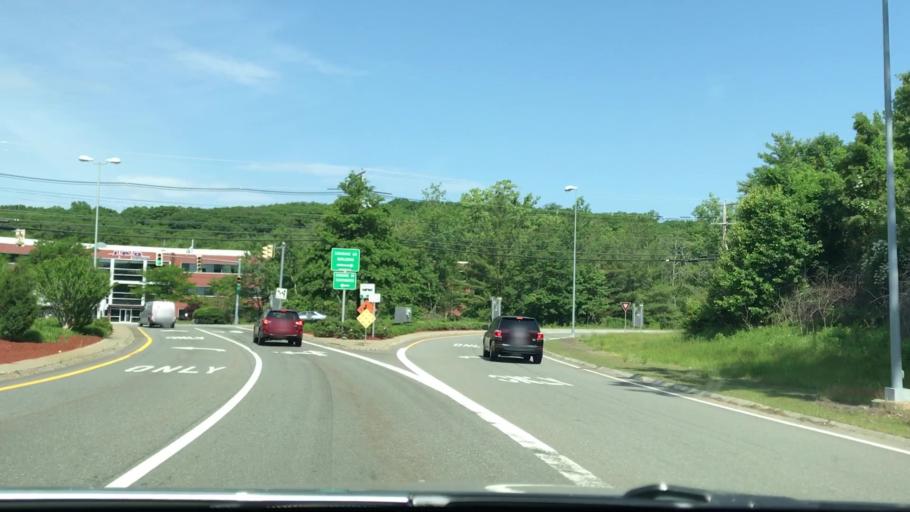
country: US
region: Massachusetts
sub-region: Middlesex County
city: Marlborough
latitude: 42.3214
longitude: -71.5781
